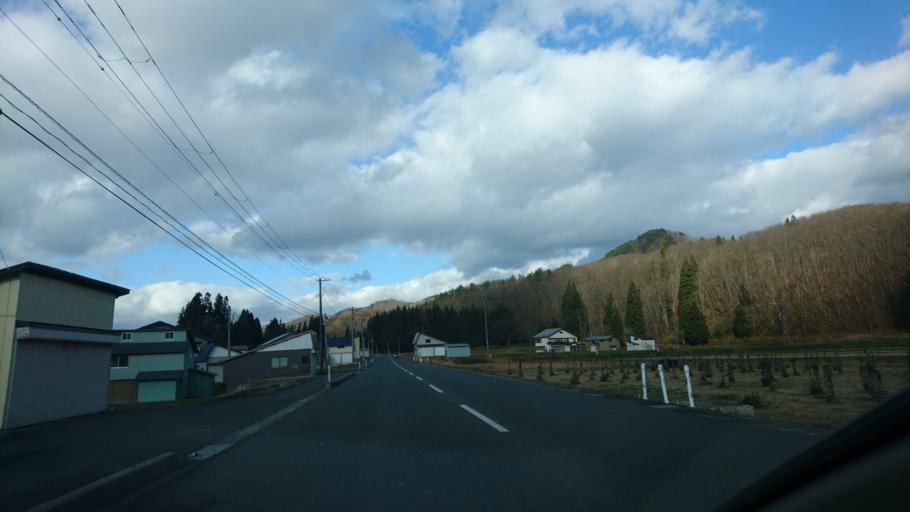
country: JP
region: Akita
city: Yokotemachi
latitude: 39.3605
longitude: 140.7702
